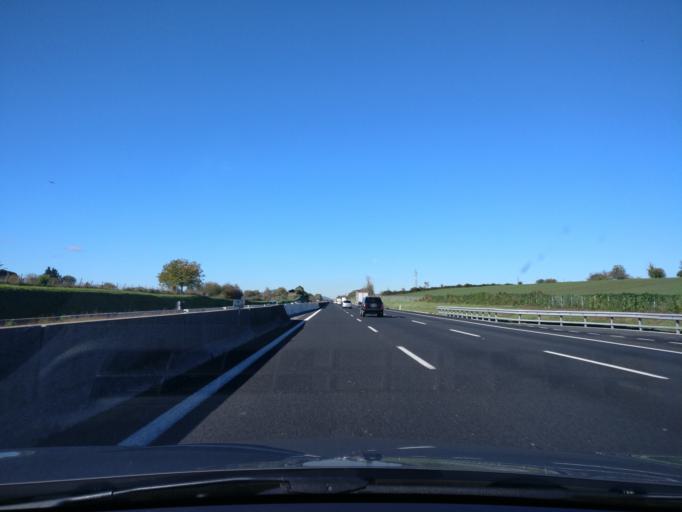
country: IT
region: Latium
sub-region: Citta metropolitana di Roma Capitale
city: Valmontone
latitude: 41.7628
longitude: 12.9401
